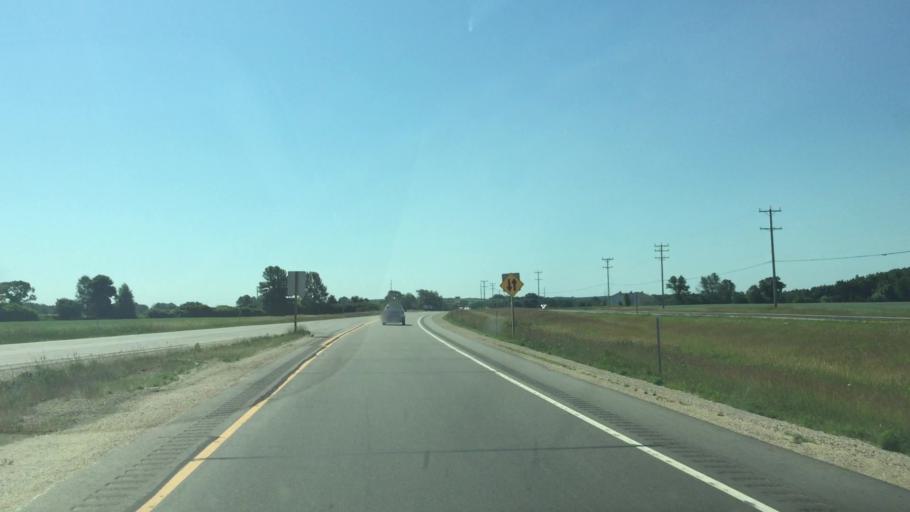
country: US
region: Wisconsin
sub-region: Outagamie County
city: Combined Locks
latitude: 44.2054
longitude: -88.3313
